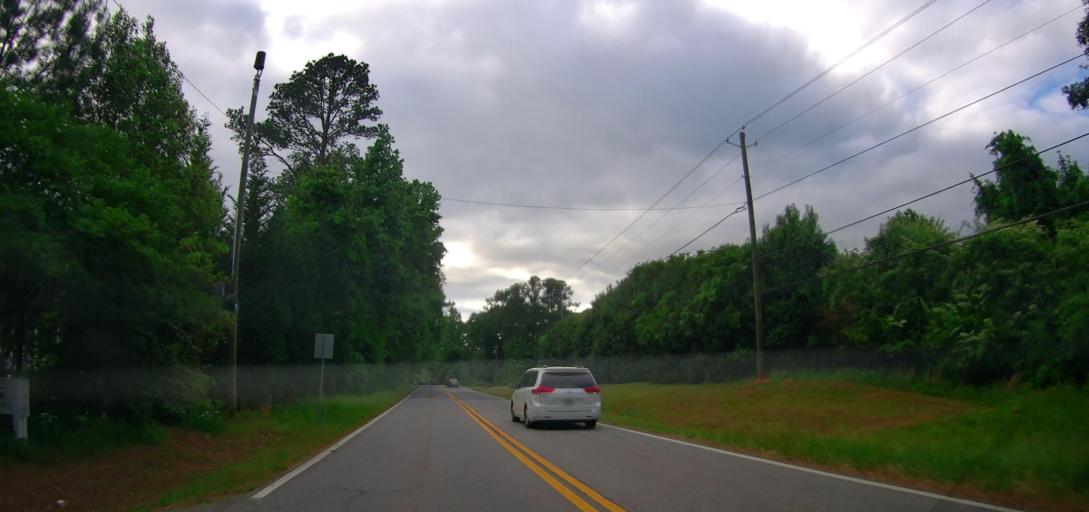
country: US
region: Georgia
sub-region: Clarke County
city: Athens
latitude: 33.9302
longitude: -83.4155
